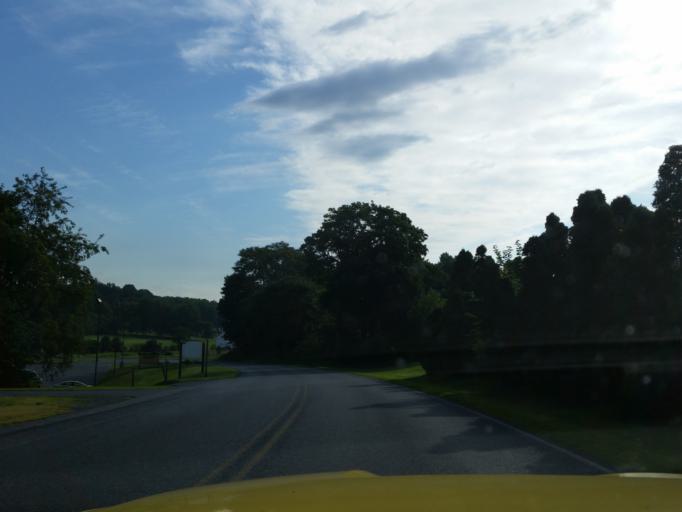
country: US
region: Pennsylvania
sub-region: Lebanon County
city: Jonestown
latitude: 40.4144
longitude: -76.4727
